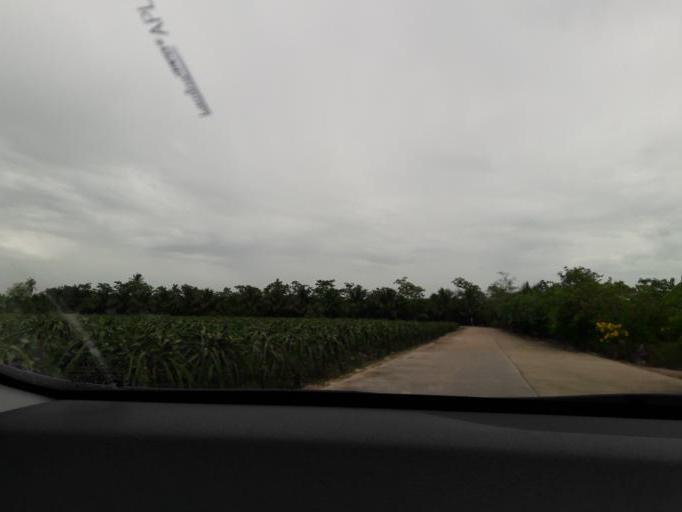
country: TH
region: Ratchaburi
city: Damnoen Saduak
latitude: 13.5532
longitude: 100.0130
